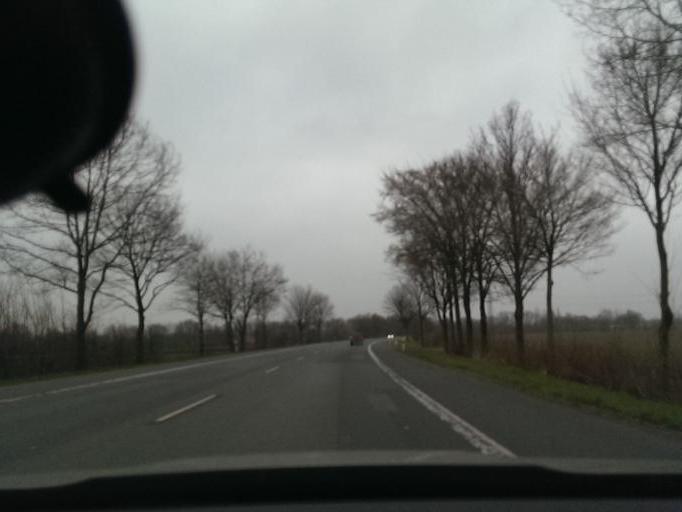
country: DE
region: North Rhine-Westphalia
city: Rietberg
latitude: 51.8159
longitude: 8.4021
